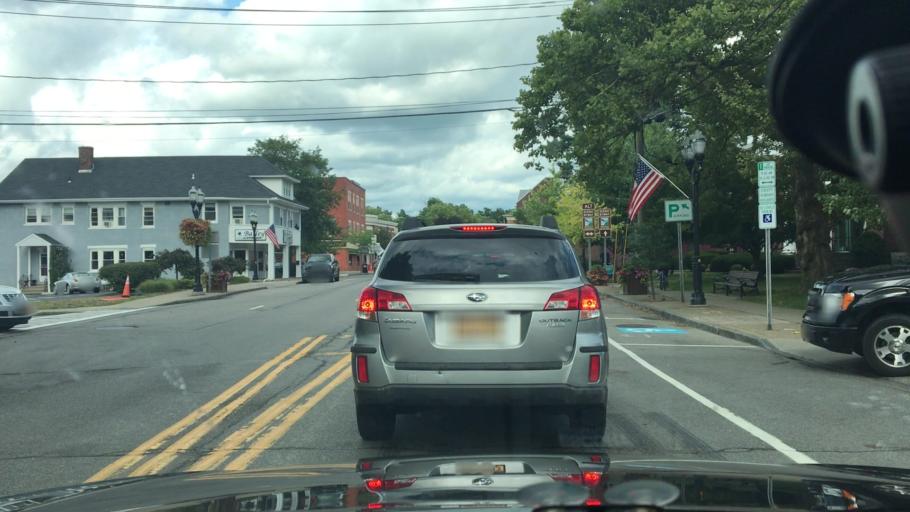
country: US
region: New York
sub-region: Erie County
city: Orchard Park
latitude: 42.7670
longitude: -78.7454
